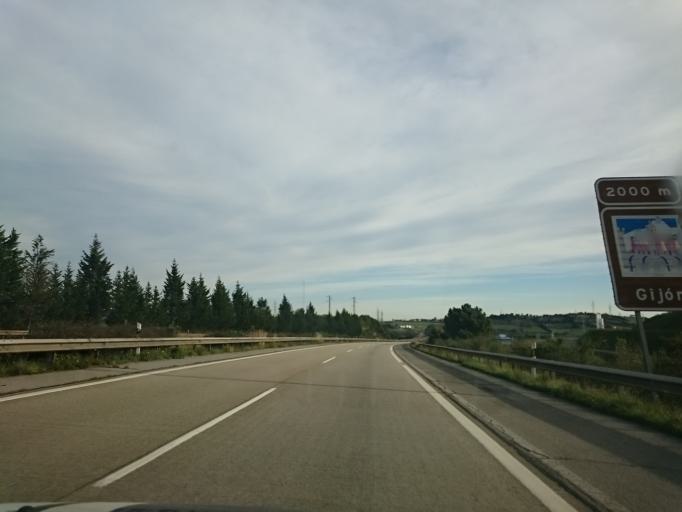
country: ES
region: Asturias
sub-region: Province of Asturias
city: Natahoyo
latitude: 43.5073
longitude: -5.7403
